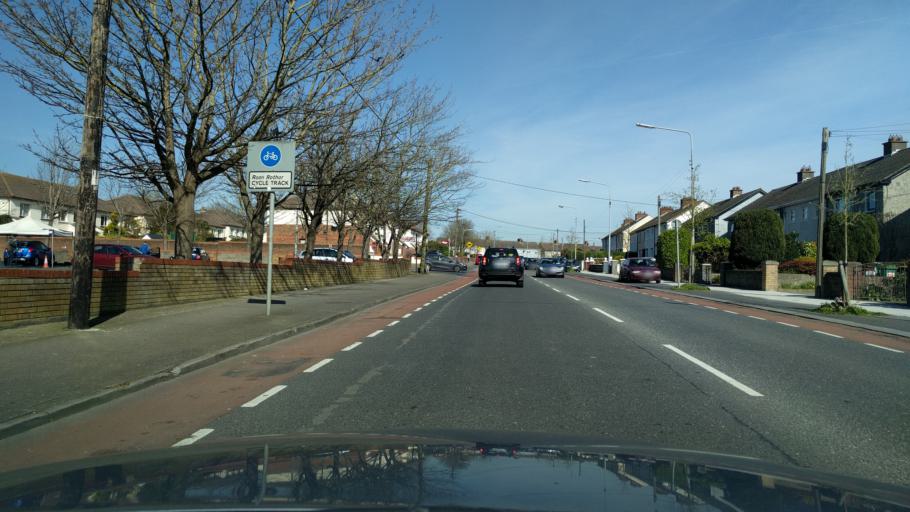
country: IE
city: Palmerstown
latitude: 53.3506
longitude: -6.3779
